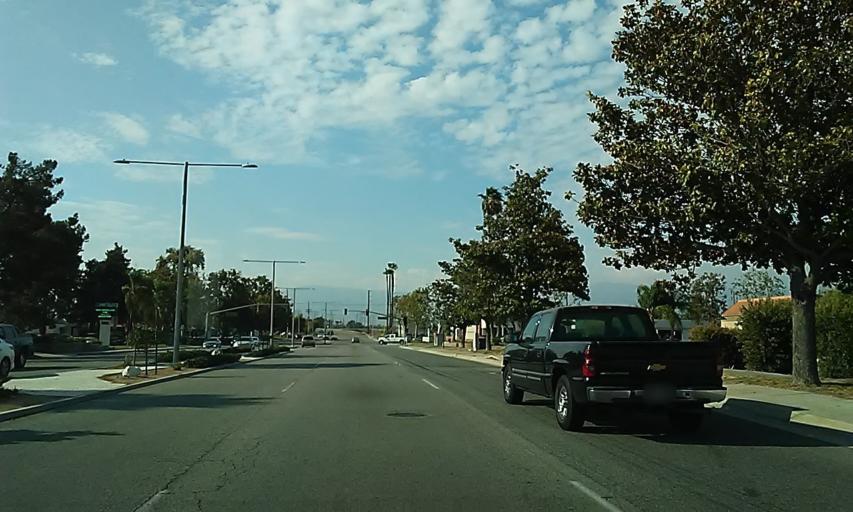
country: US
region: California
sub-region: San Bernardino County
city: Grand Terrace
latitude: 34.0533
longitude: -117.3091
